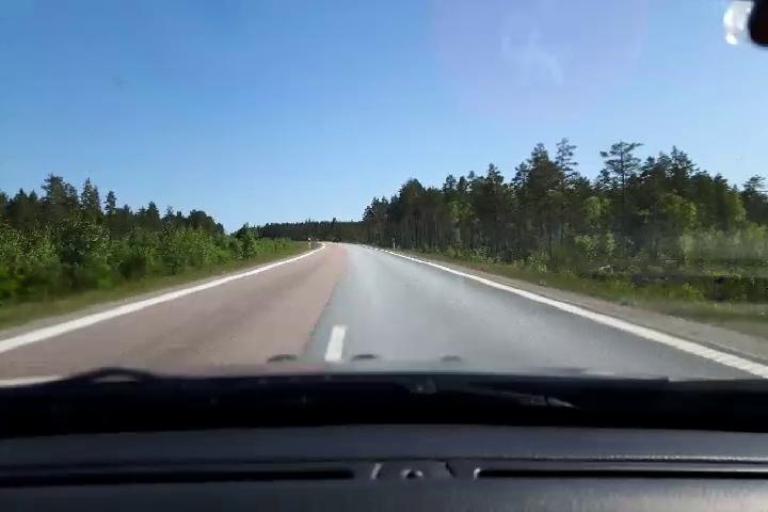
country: SE
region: Gaevleborg
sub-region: Soderhamns Kommun
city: Soderhamn
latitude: 61.3786
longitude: 16.9942
